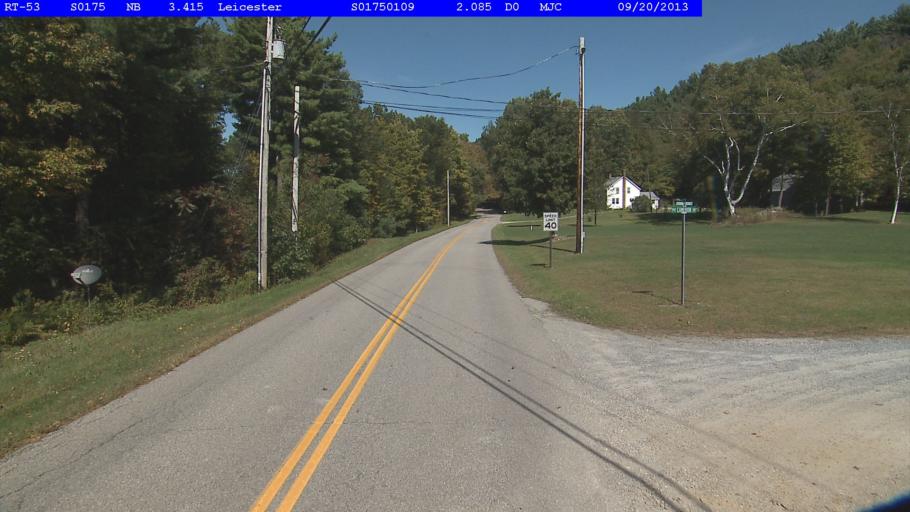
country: US
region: Vermont
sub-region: Rutland County
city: Brandon
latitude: 43.8729
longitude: -73.0644
